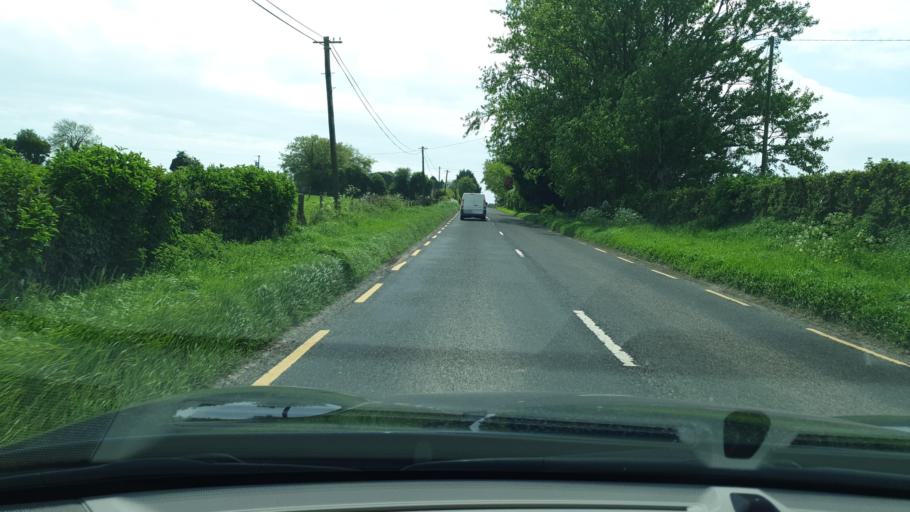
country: IE
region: Leinster
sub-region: An Mhi
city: Navan
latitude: 53.7824
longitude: -6.7298
